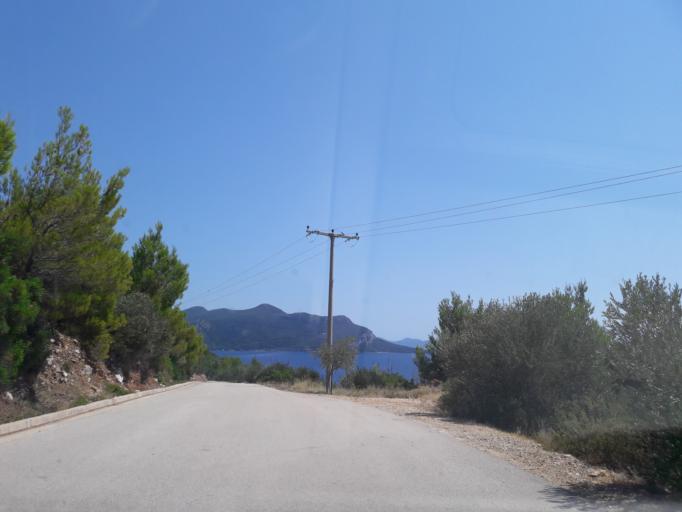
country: HR
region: Dubrovacko-Neretvanska
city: Blato
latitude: 42.9149
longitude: 17.4118
